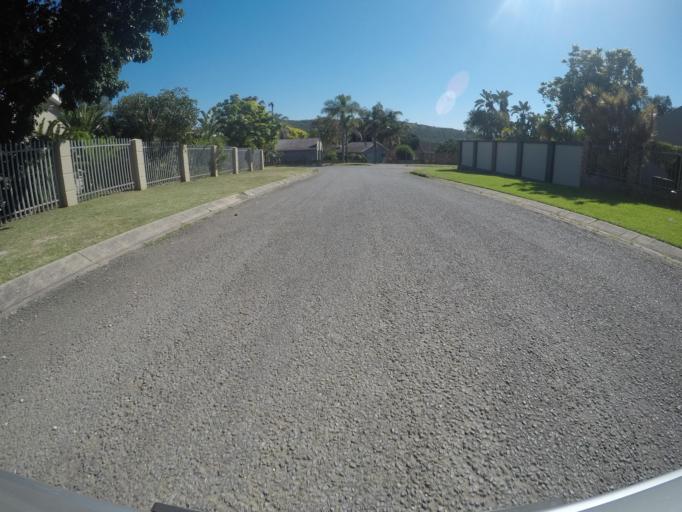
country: ZA
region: Eastern Cape
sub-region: Buffalo City Metropolitan Municipality
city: East London
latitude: -32.9455
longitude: 27.8996
